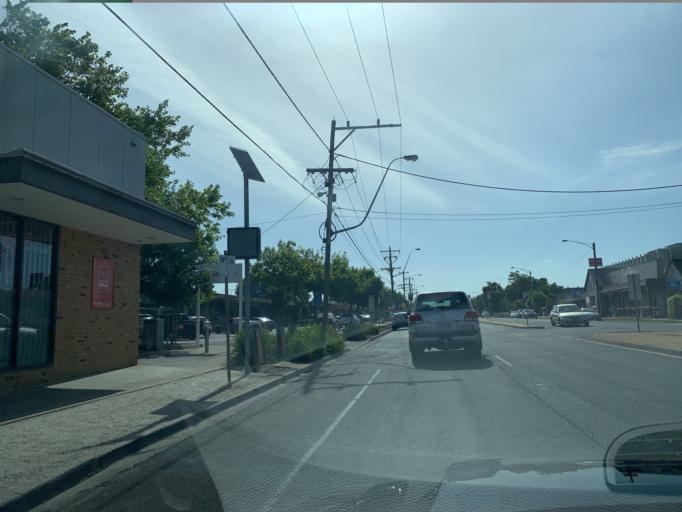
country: AU
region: Victoria
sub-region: Ballarat North
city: Newington
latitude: -37.5402
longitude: 143.8303
